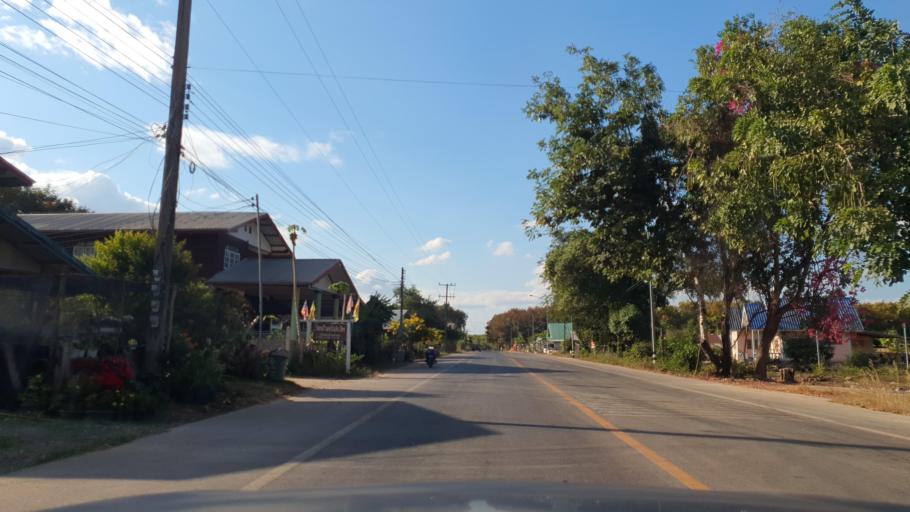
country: TH
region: Nong Khai
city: Bueng Khong Long
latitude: 18.0120
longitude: 104.0062
